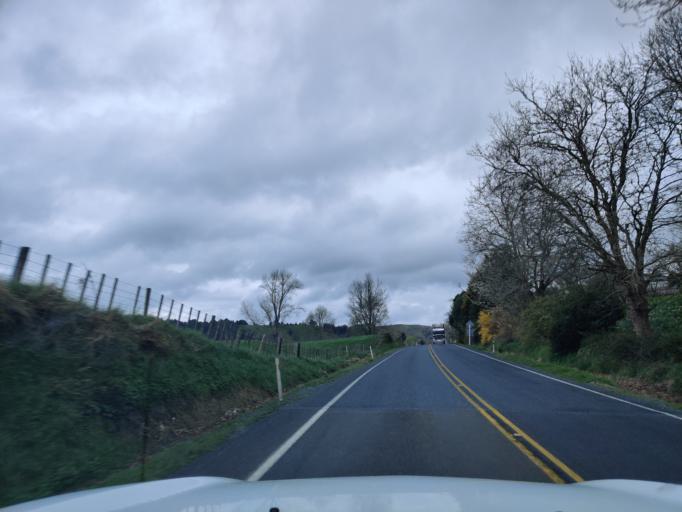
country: NZ
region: Waikato
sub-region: Otorohanga District
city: Otorohanga
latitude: -38.5220
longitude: 175.1779
